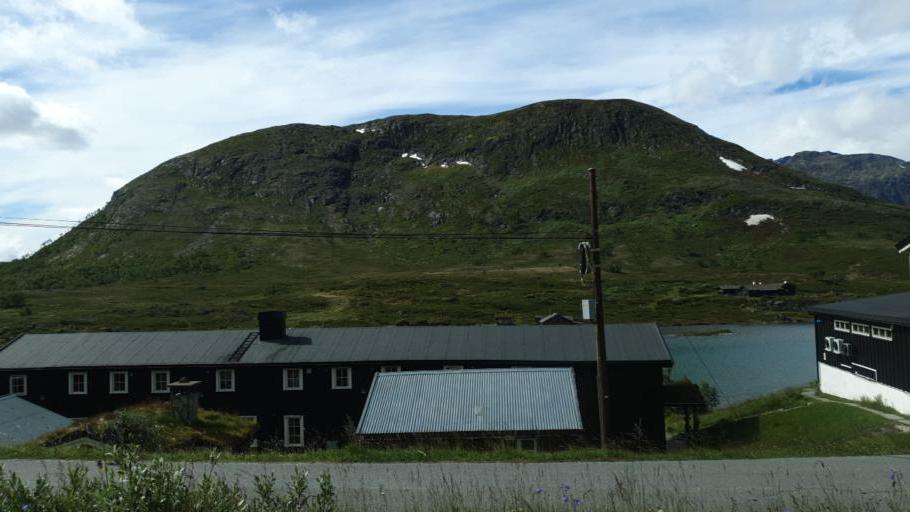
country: NO
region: Oppland
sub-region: Lom
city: Fossbergom
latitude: 61.4943
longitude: 8.8134
